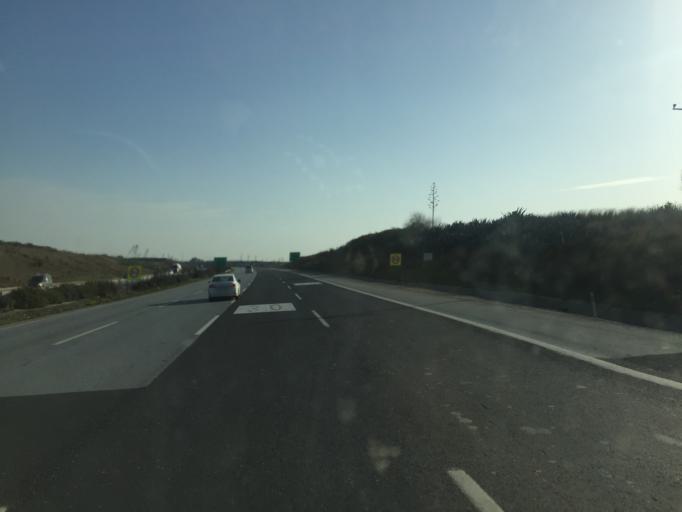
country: TR
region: Mersin
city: Yenice
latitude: 37.0232
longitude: 35.0961
